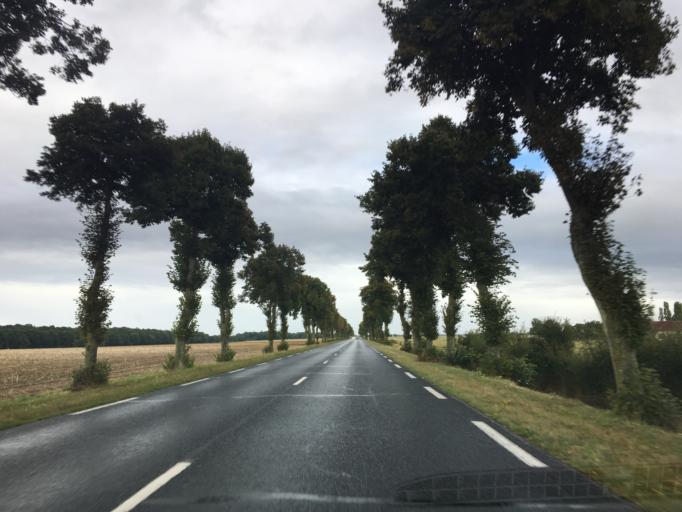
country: FR
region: Haute-Normandie
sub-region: Departement de l'Eure
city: Francheville
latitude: 48.7423
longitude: 0.8657
